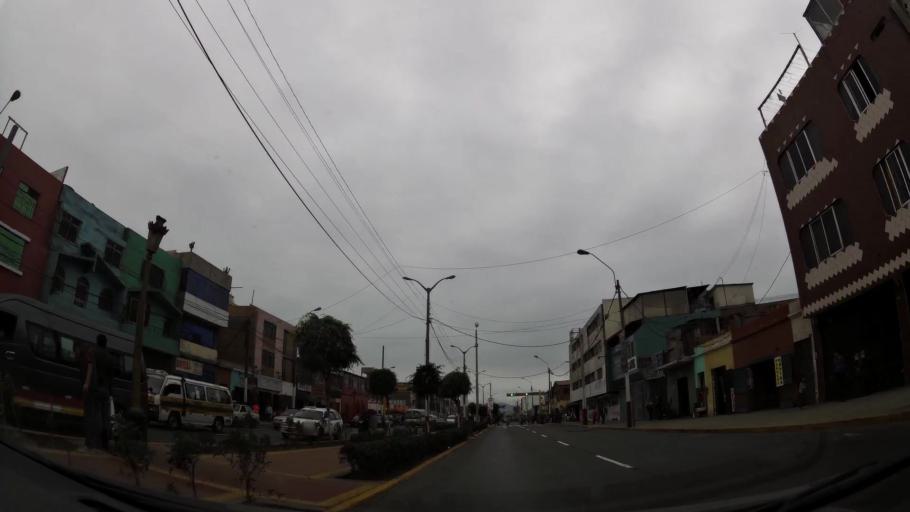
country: PE
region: Callao
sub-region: Callao
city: Callao
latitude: -12.0621
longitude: -77.1376
